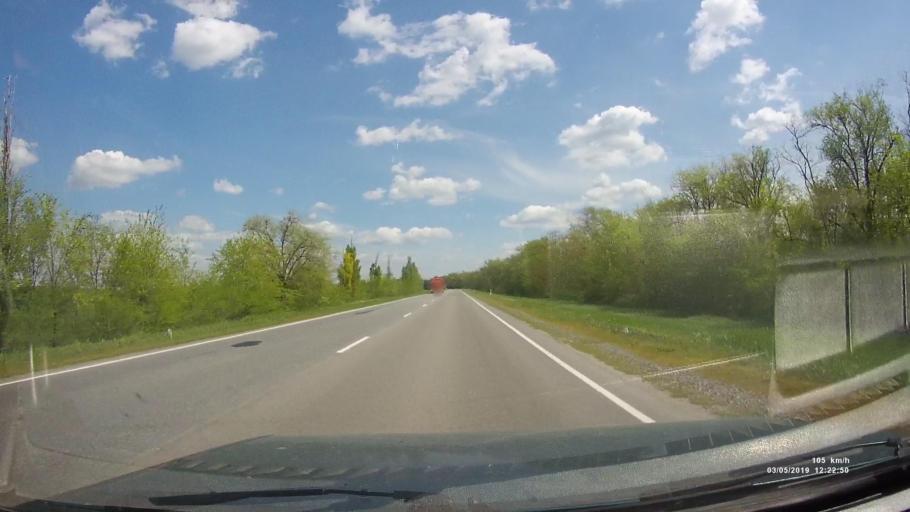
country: RU
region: Rostov
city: Semikarakorsk
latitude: 47.4064
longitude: 40.6702
